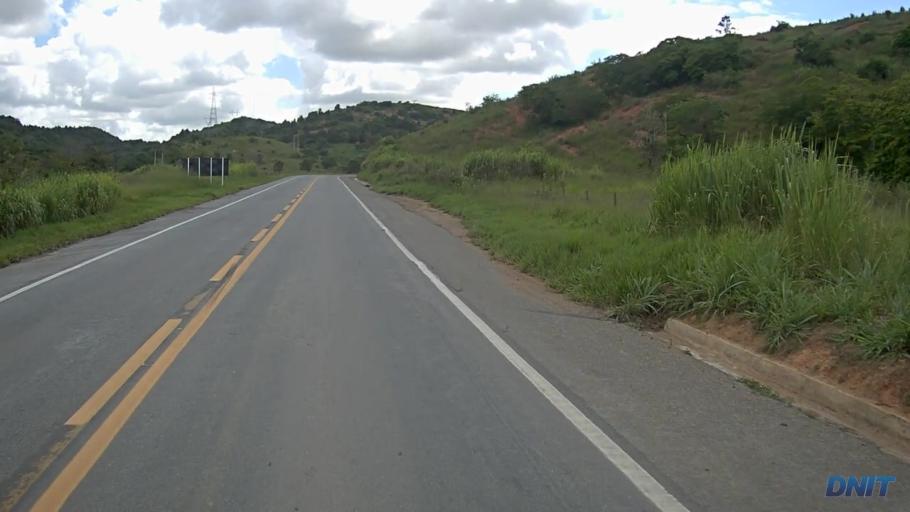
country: BR
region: Minas Gerais
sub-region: Governador Valadares
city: Governador Valadares
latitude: -18.9688
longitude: -42.0919
